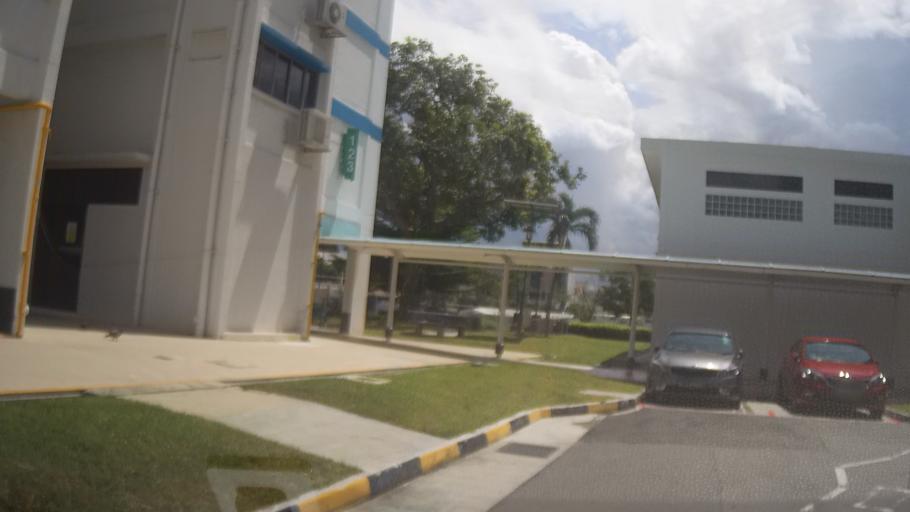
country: SG
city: Singapore
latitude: 1.3226
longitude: 103.8834
